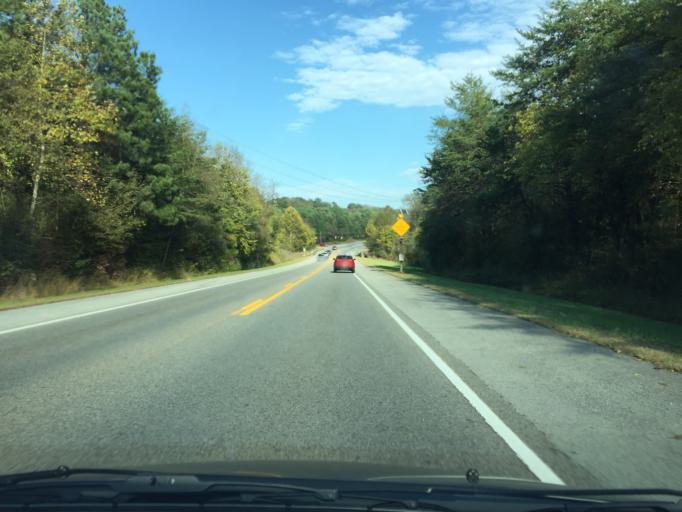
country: US
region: Tennessee
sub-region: Loudon County
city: Loudon
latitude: 35.7194
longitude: -84.3510
